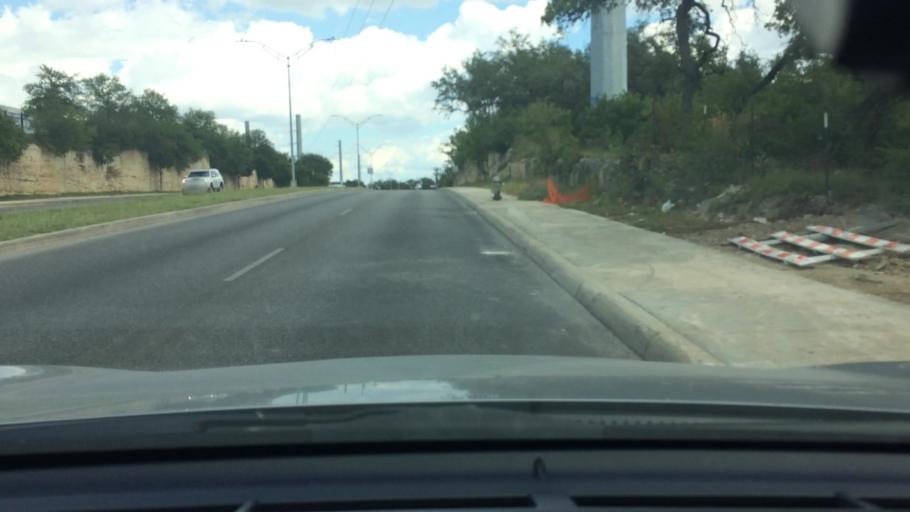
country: US
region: Texas
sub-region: Bexar County
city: Leon Valley
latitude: 29.4804
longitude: -98.6983
